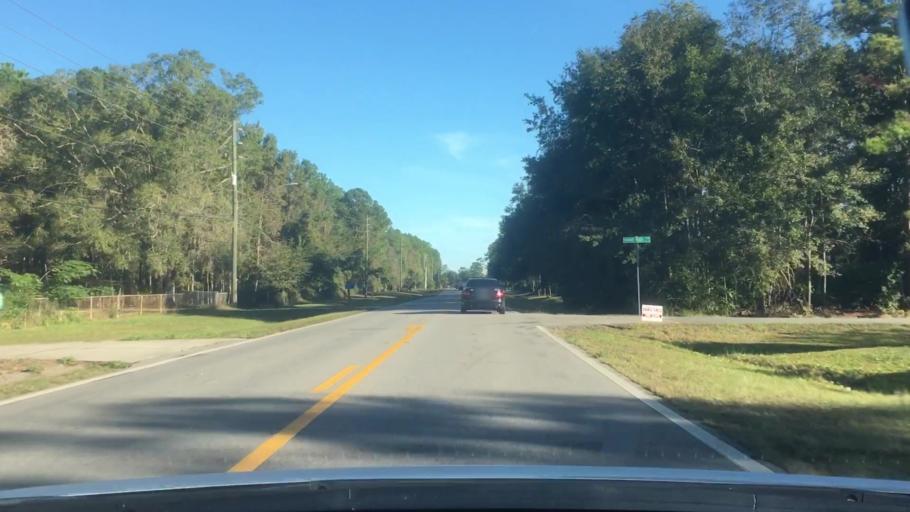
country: US
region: Florida
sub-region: Nassau County
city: Yulee
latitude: 30.4837
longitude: -81.5766
